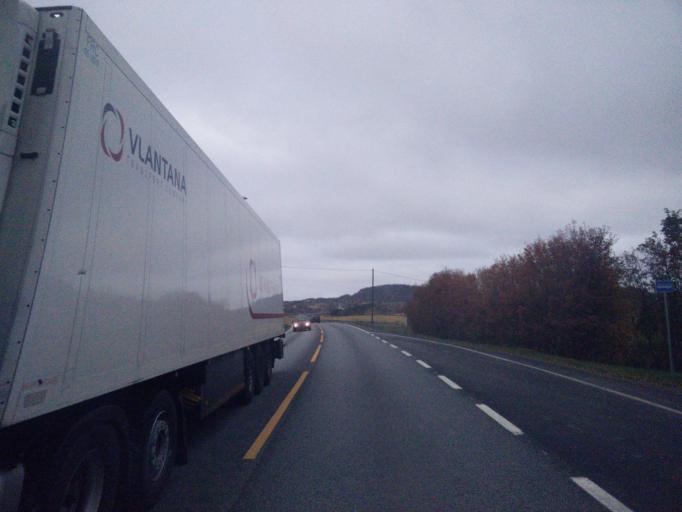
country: NO
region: Nord-Trondelag
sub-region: Stjordal
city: Stjordal
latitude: 63.4970
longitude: 10.8793
